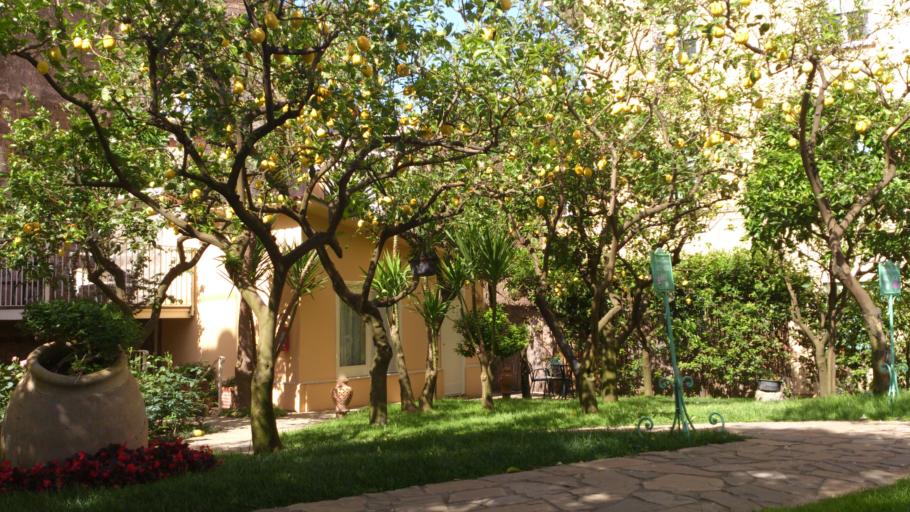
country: IT
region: Campania
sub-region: Provincia di Napoli
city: Sorrento
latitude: 40.6251
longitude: 14.3752
